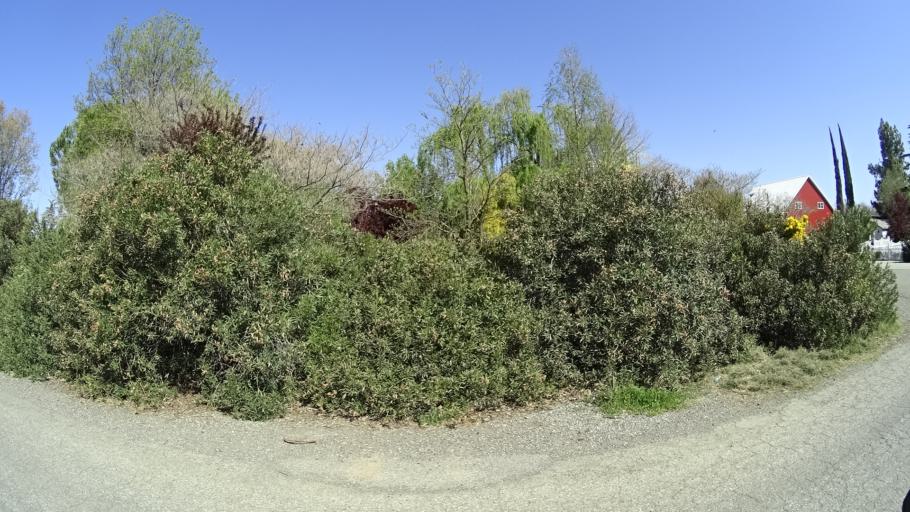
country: US
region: California
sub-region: Glenn County
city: Willows
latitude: 39.4282
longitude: -122.0194
